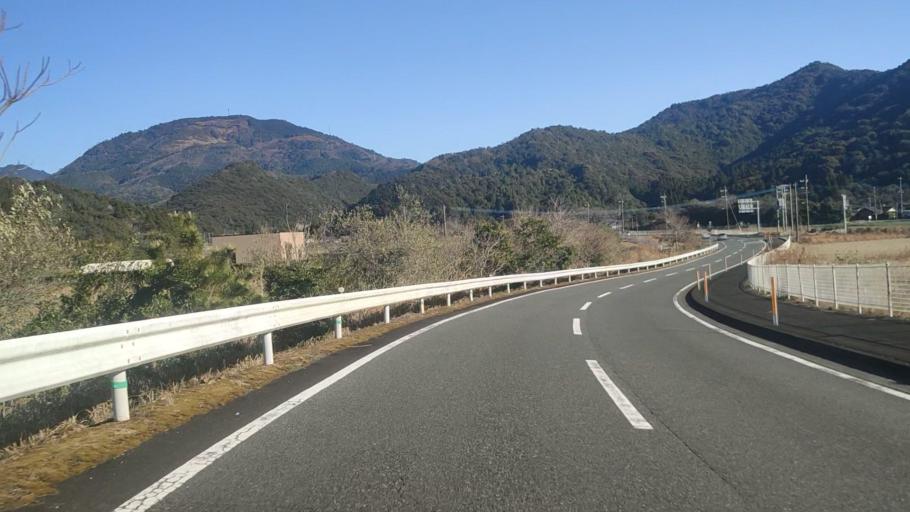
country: JP
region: Miyazaki
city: Nobeoka
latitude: 32.6785
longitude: 131.7841
